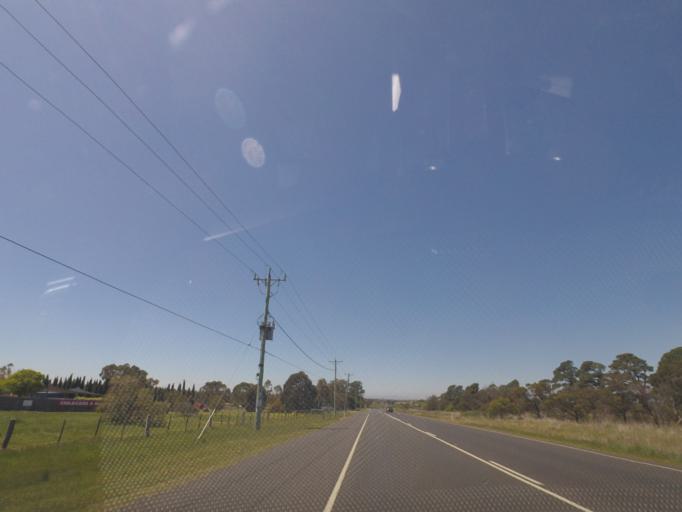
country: AU
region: Victoria
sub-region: Hume
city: Sunbury
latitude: -37.4670
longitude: 144.6616
